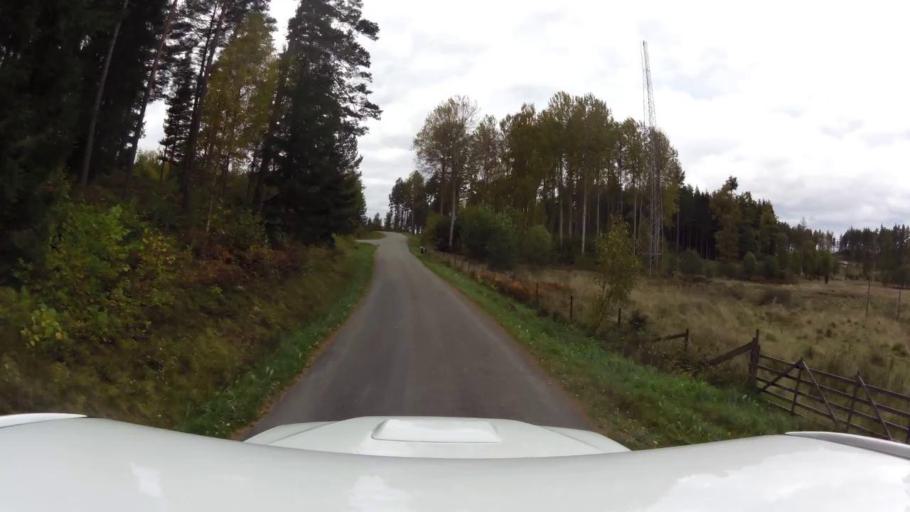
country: SE
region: OEstergoetland
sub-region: Kinda Kommun
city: Rimforsa
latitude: 58.1956
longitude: 15.5854
